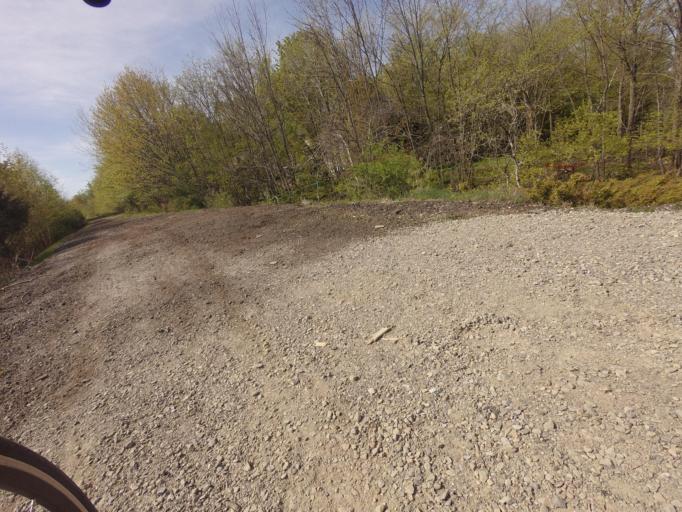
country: CA
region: Ontario
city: Arnprior
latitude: 45.4643
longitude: -76.2853
